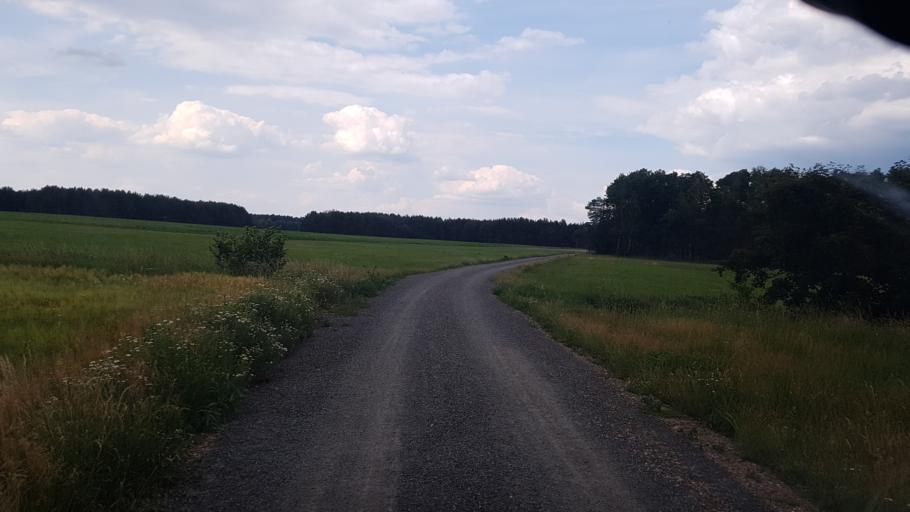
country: DE
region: Brandenburg
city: Plessa
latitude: 51.5409
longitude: 13.6397
